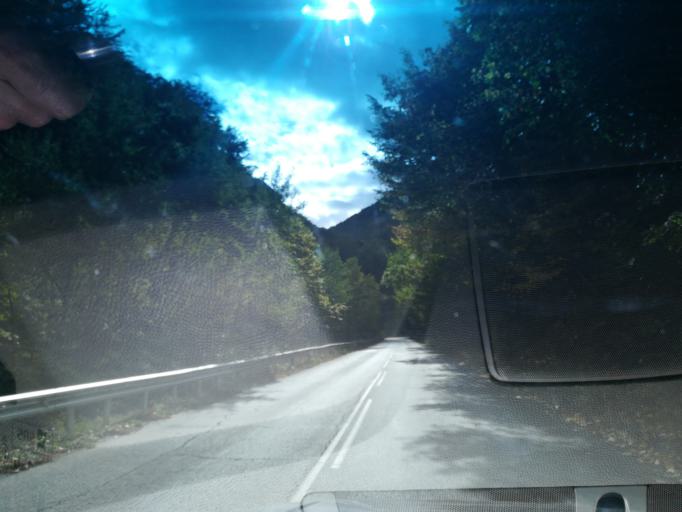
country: BG
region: Pazardzhik
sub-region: Obshtina Peshtera
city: Peshtera
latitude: 42.0004
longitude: 24.2541
